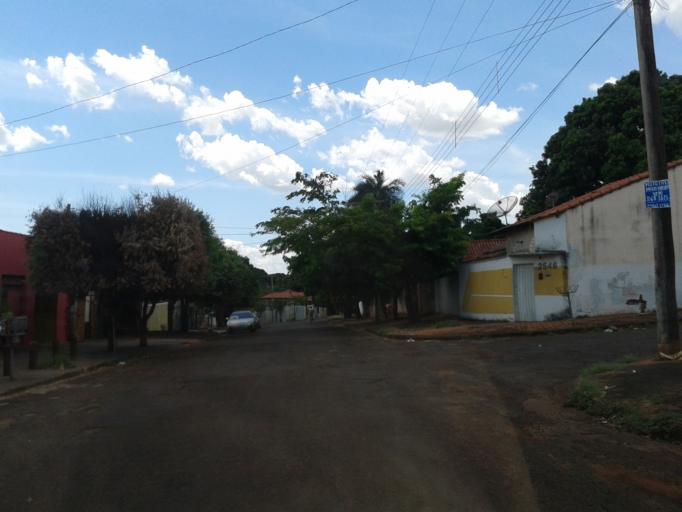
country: BR
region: Minas Gerais
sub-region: Ituiutaba
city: Ituiutaba
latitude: -18.9842
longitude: -49.4731
